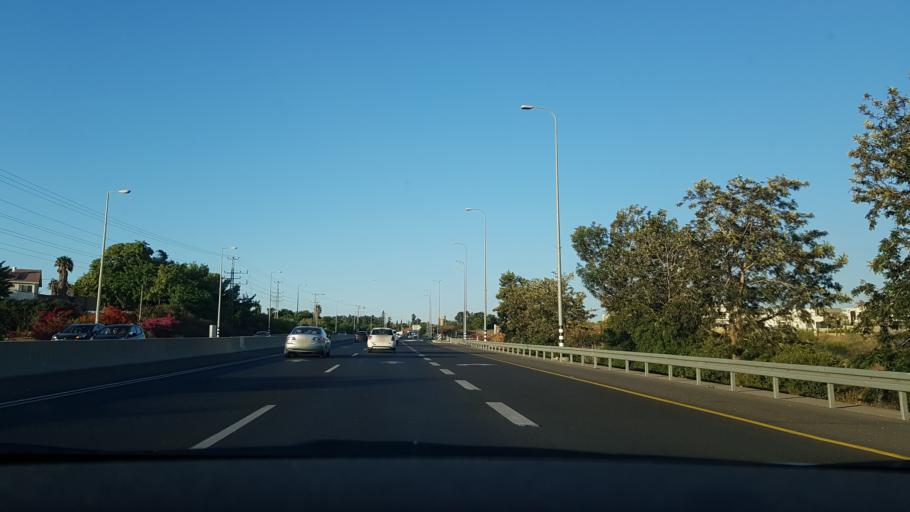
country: IL
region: Central District
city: Ness Ziona
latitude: 31.9275
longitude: 34.7732
